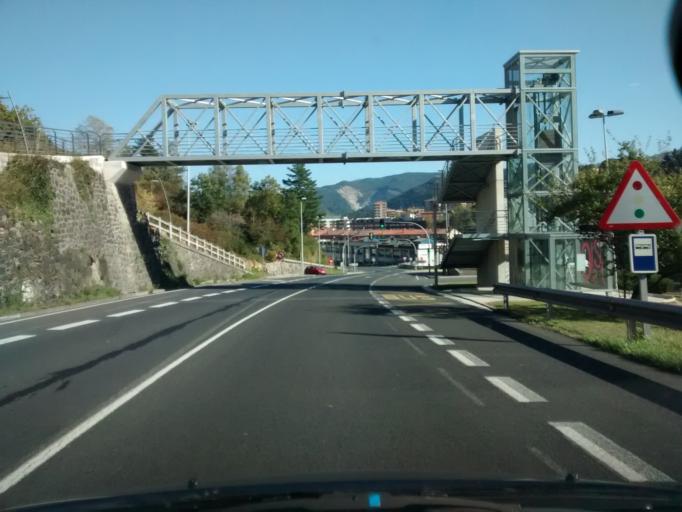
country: ES
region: Basque Country
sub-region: Provincia de Guipuzcoa
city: Elgoibar
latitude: 43.2091
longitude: -2.4219
